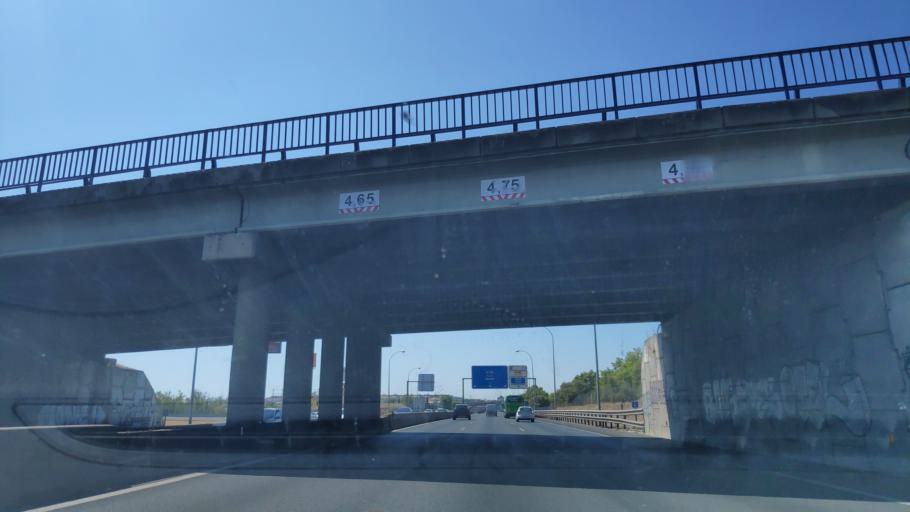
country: ES
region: Madrid
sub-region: Provincia de Madrid
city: Getafe
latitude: 40.2857
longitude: -3.7442
